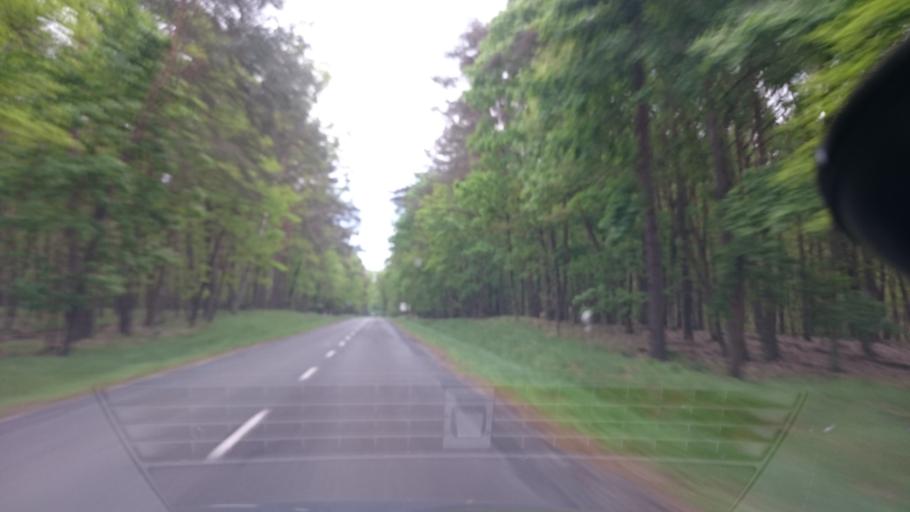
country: PL
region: Kujawsko-Pomorskie
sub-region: Grudziadz
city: Grudziadz
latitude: 53.4452
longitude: 18.7746
